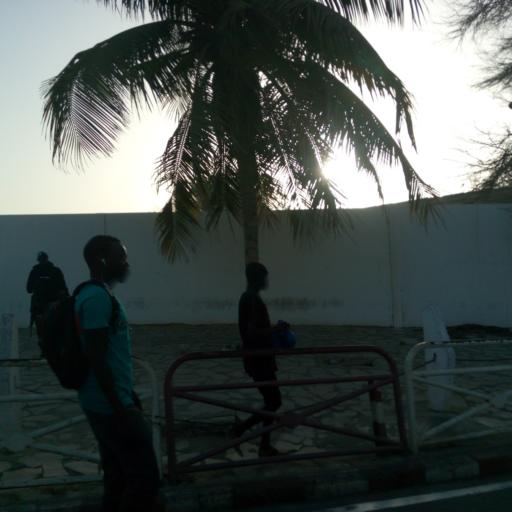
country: SN
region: Dakar
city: Dakar
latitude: 14.6902
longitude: -17.4467
